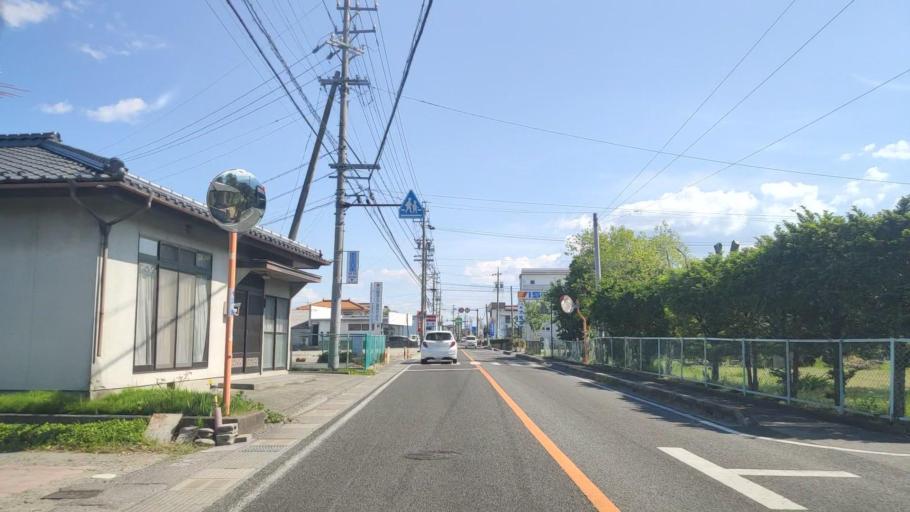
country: JP
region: Nagano
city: Toyoshina
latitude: 36.2898
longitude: 137.9073
